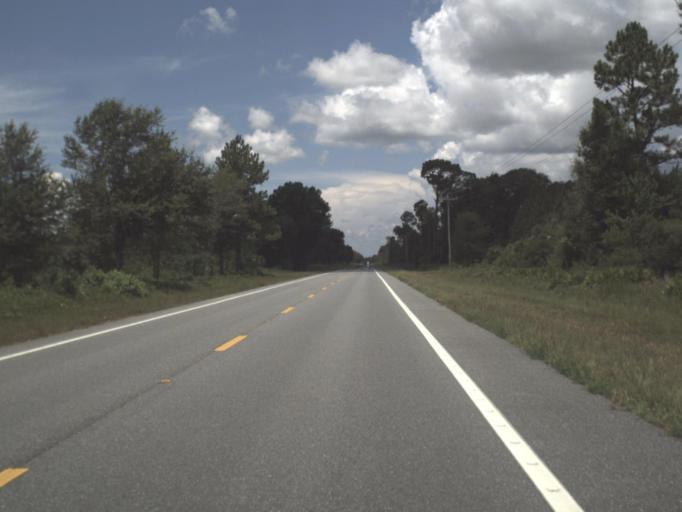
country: US
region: Florida
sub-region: Taylor County
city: Perry
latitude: 30.1428
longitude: -83.8236
